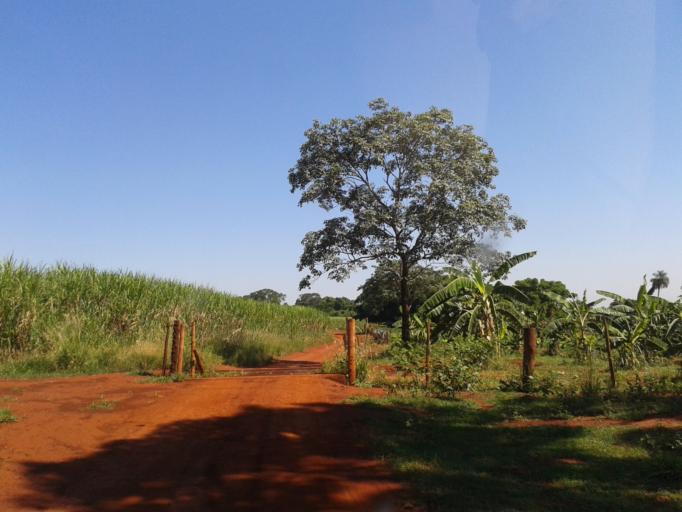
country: BR
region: Minas Gerais
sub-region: Centralina
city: Centralina
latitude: -18.6377
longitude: -49.2982
